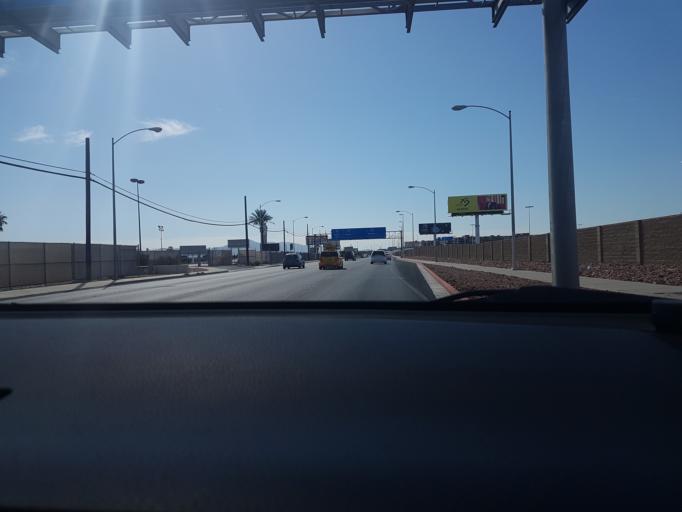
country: US
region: Nevada
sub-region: Clark County
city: Paradise
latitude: 36.0969
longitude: -115.1487
